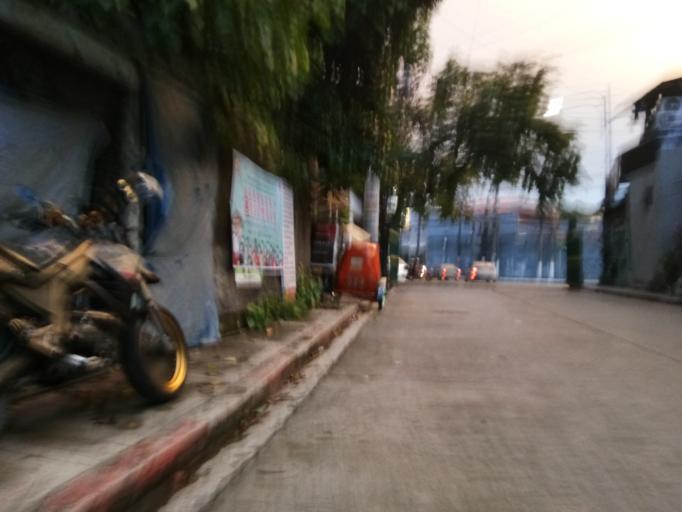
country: PH
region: Metro Manila
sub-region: San Juan
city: San Juan
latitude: 14.6100
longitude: 121.0427
